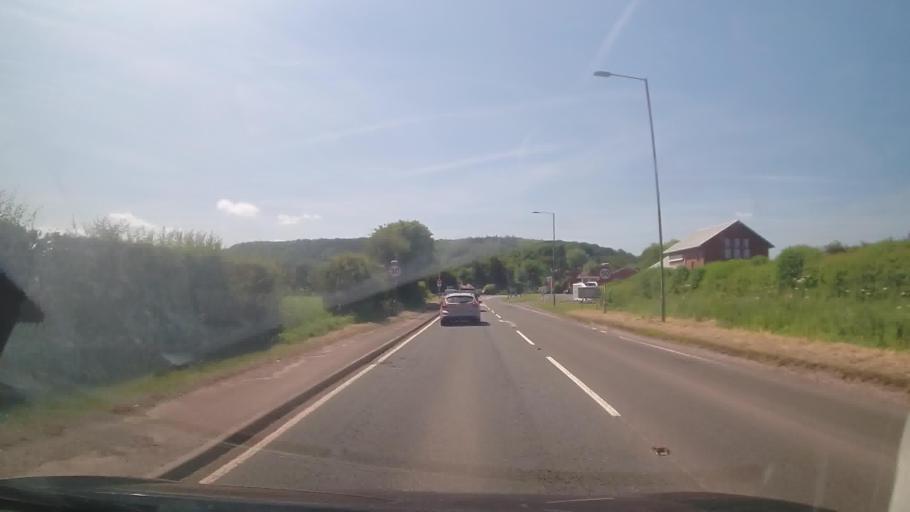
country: GB
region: England
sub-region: Herefordshire
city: Hope under Dinmore
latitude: 52.1758
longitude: -2.7147
